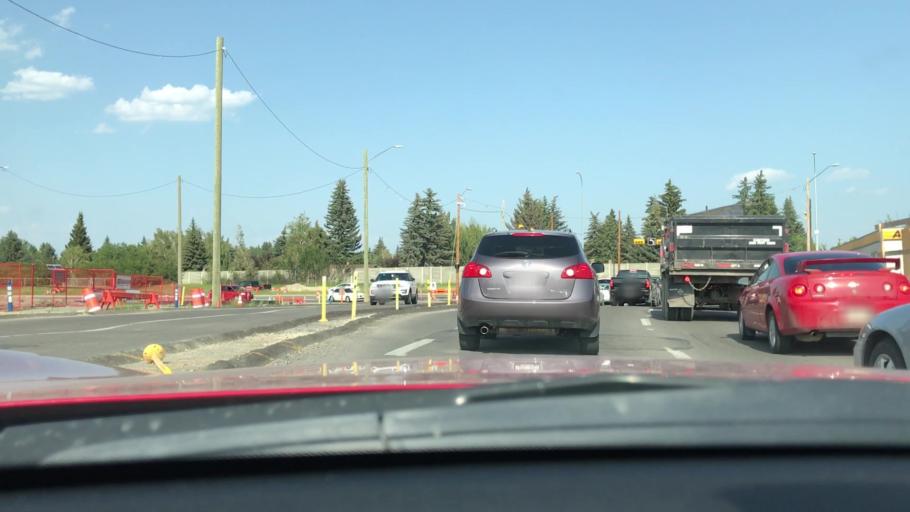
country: CA
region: Alberta
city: Calgary
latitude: 50.9724
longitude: -114.0964
